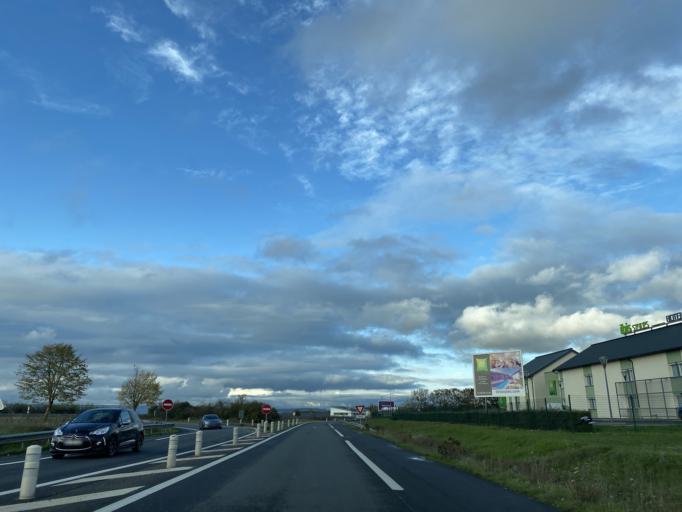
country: FR
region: Centre
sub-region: Departement du Cher
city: La Chapelle-Saint-Ursin
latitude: 47.0485
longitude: 2.3445
